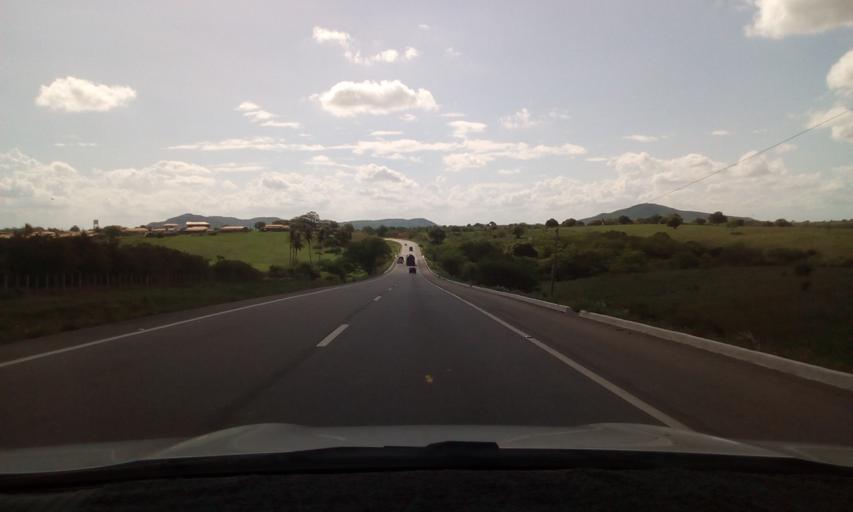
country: BR
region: Paraiba
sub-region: Gurinhem
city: Gurinhem
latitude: -7.1640
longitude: -35.3420
